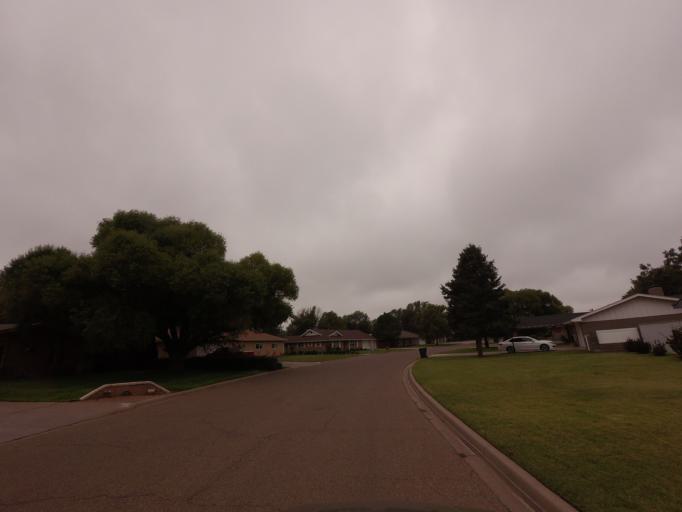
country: US
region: New Mexico
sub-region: Curry County
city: Clovis
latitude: 34.4354
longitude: -103.1860
